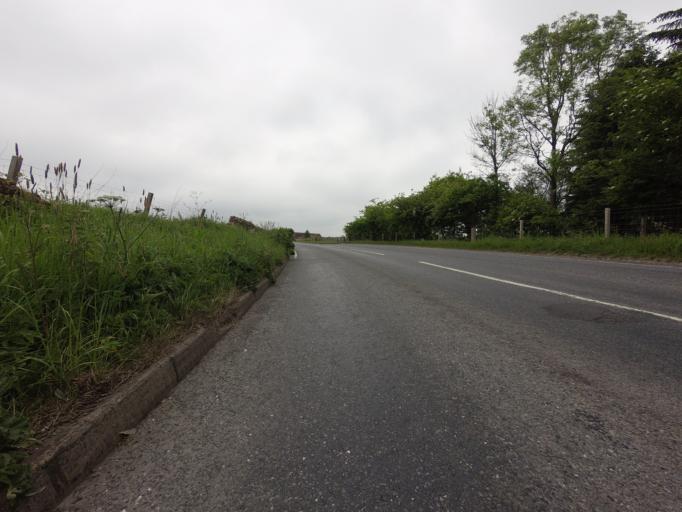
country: GB
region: Scotland
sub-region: Fife
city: Townhill
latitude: 56.1212
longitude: -3.4390
